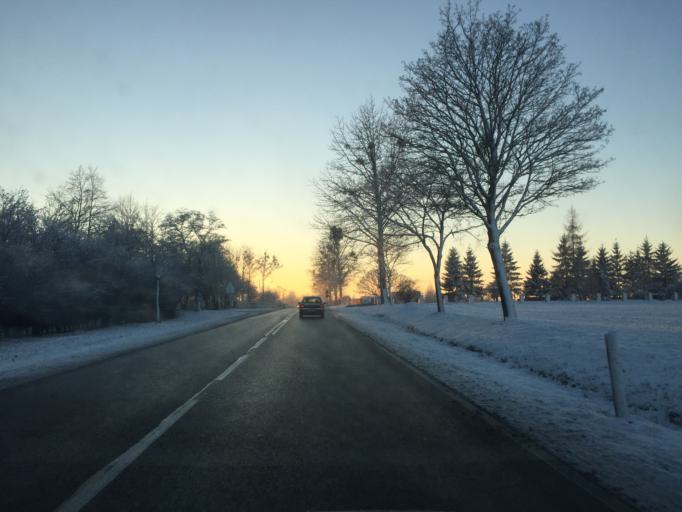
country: PL
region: Kujawsko-Pomorskie
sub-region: Powiat torunski
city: Lubicz Gorny
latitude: 53.1051
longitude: 18.7949
